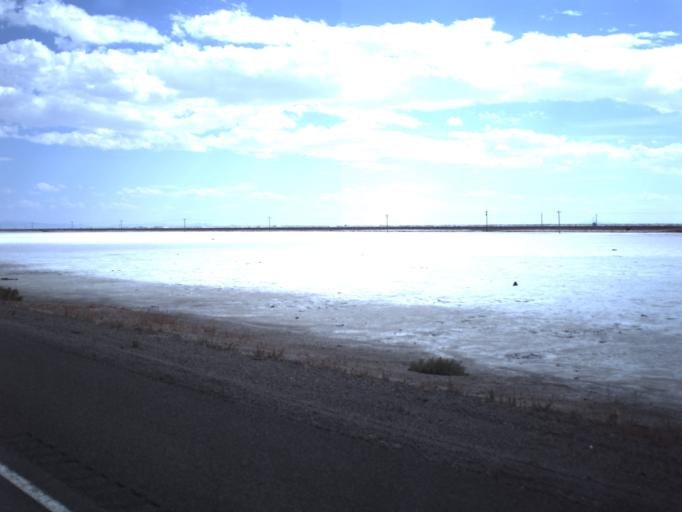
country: US
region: Utah
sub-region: Tooele County
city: Wendover
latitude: 40.7383
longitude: -113.8443
